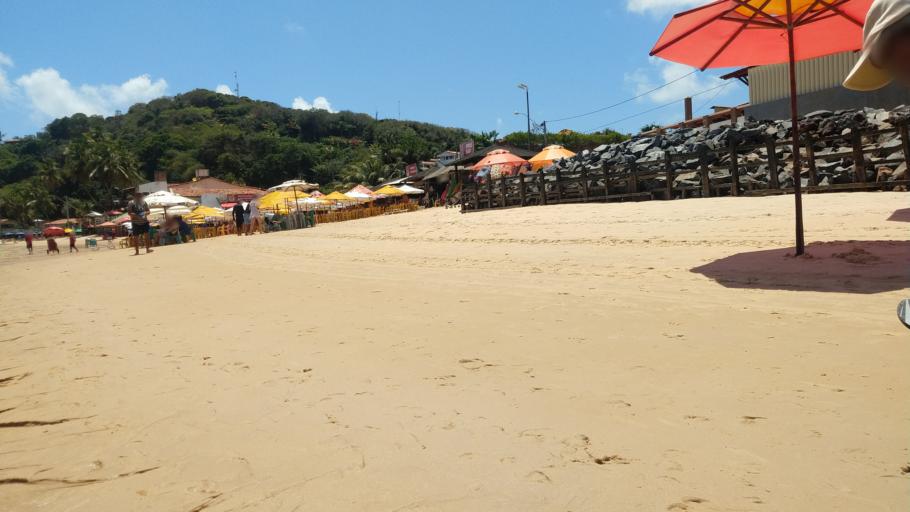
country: BR
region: Rio Grande do Norte
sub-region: Ares
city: Ares
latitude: -6.2276
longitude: -35.0483
